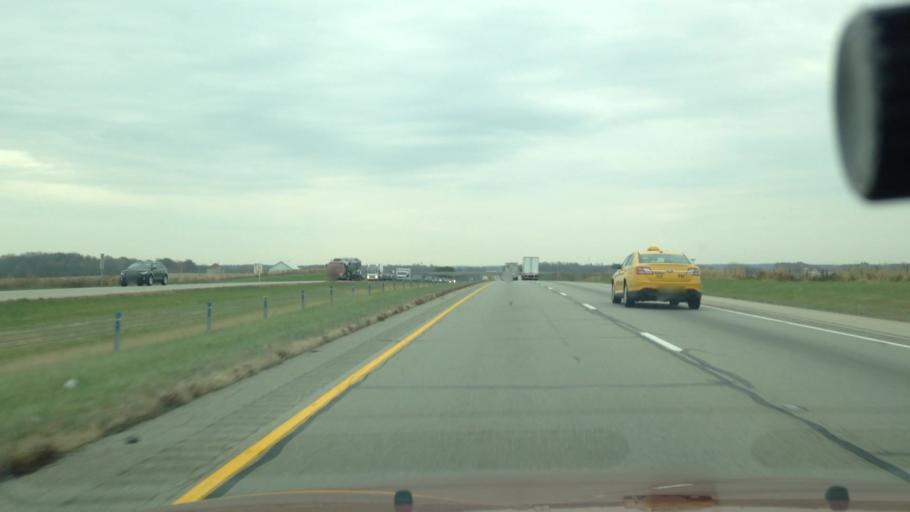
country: US
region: Indiana
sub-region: Wayne County
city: Cambridge City
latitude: 39.8532
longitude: -85.1893
